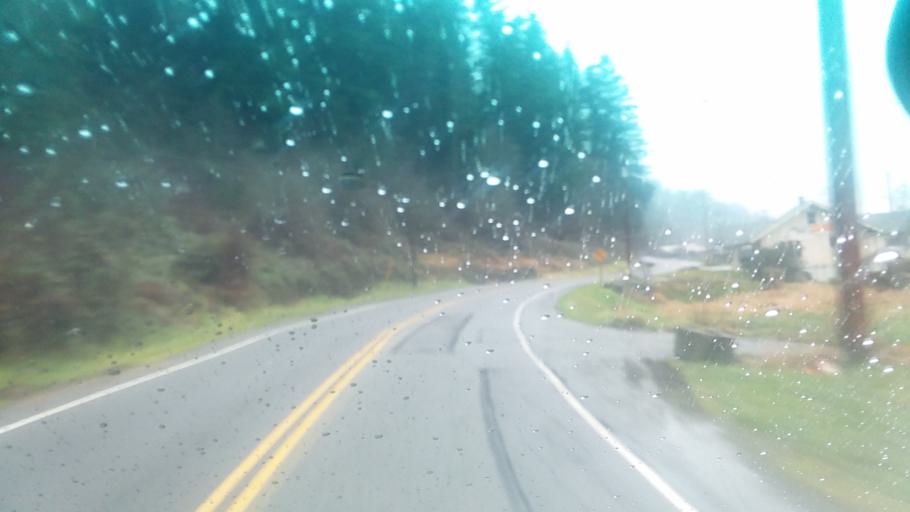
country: US
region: Washington
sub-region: King County
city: Pacific
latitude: 47.2587
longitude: -122.2629
